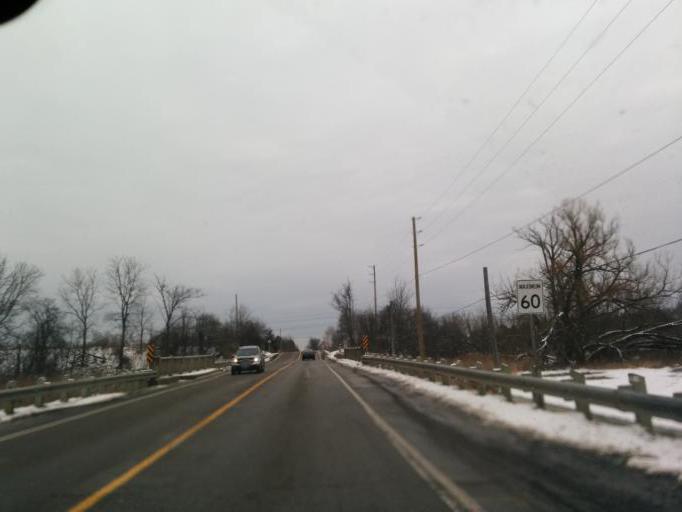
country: CA
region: Ontario
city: Etobicoke
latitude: 43.7633
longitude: -79.6513
